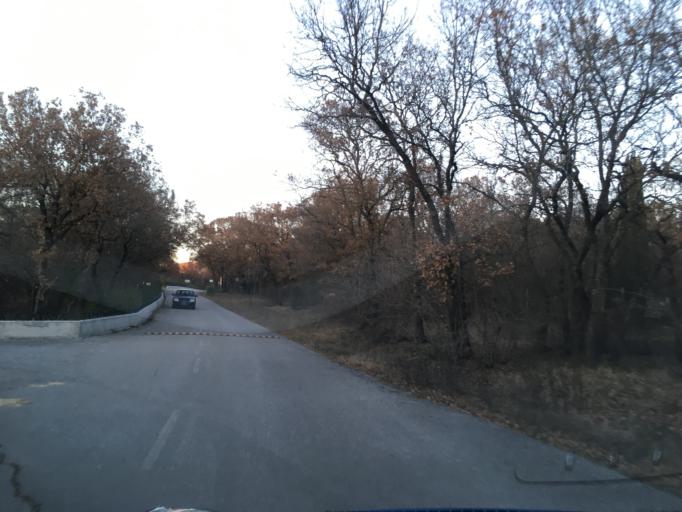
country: GR
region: West Macedonia
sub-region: Nomos Kozanis
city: Koila
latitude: 40.3259
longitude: 21.8314
